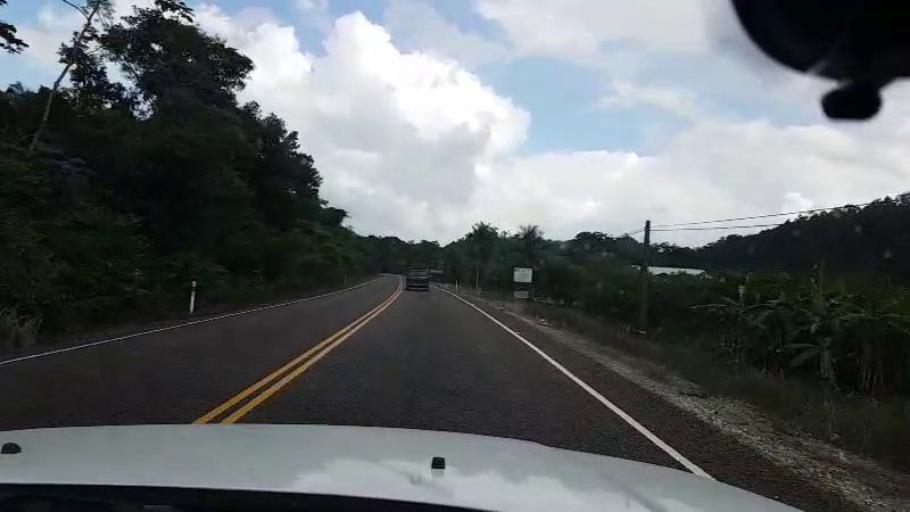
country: BZ
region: Cayo
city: Belmopan
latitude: 17.1516
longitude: -88.6684
